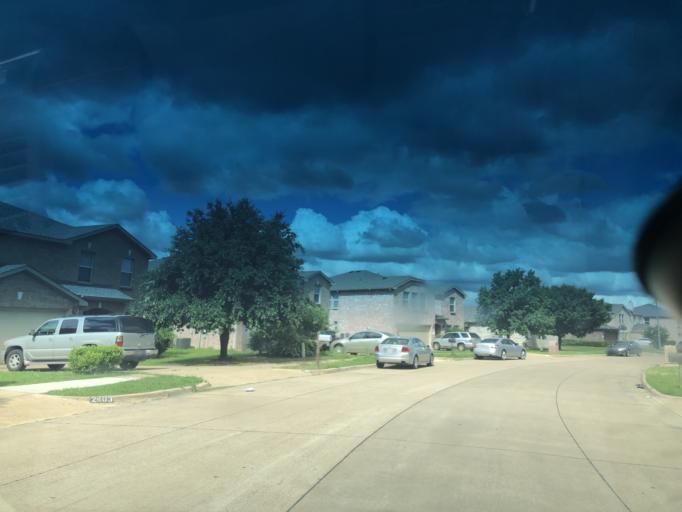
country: US
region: Texas
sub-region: Dallas County
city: Grand Prairie
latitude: 32.7036
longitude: -97.0380
